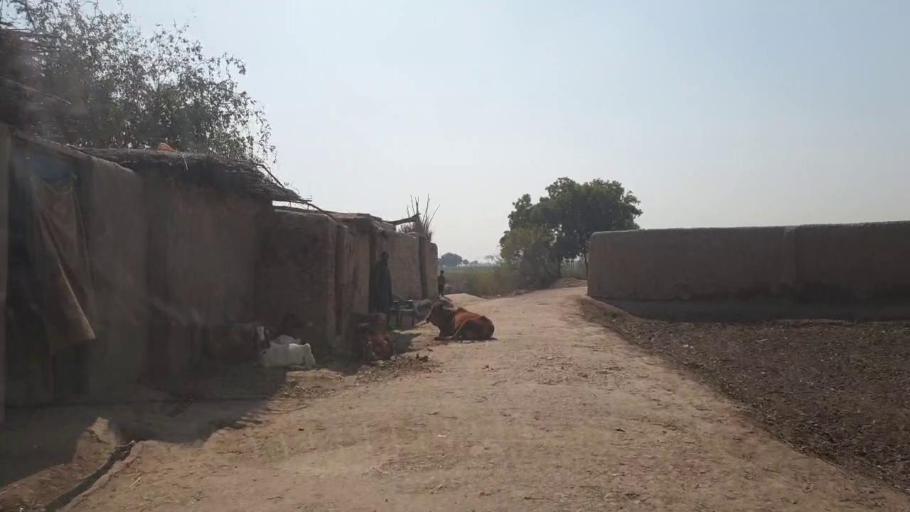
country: PK
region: Sindh
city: Tando Jam
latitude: 25.3263
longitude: 68.6376
